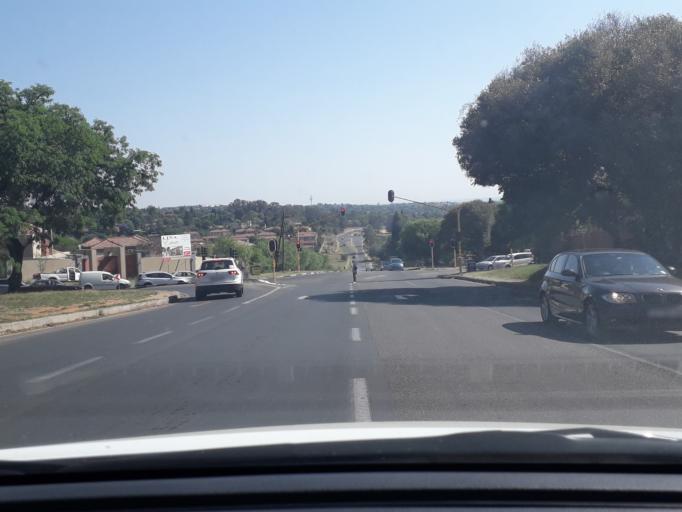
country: ZA
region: Gauteng
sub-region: City of Johannesburg Metropolitan Municipality
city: Roodepoort
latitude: -26.0839
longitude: 27.9573
